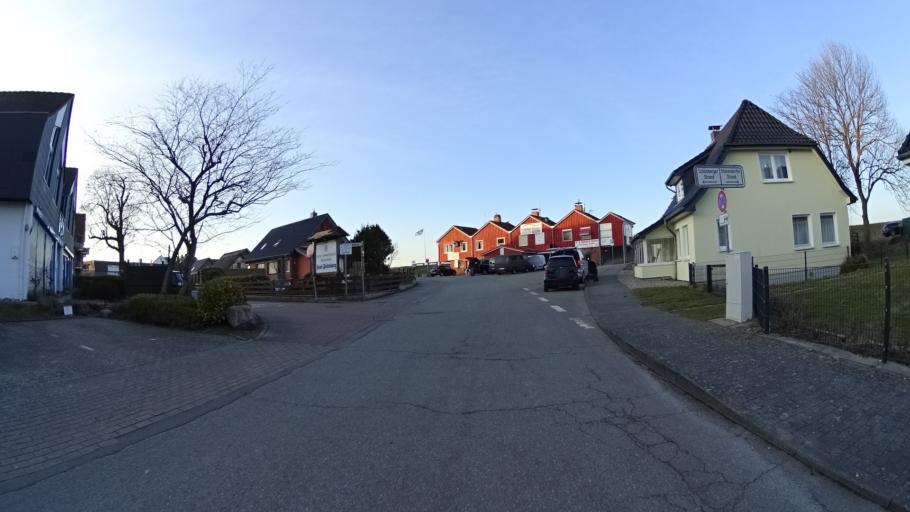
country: DE
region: Schleswig-Holstein
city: Stakendorf
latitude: 54.4105
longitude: 10.4206
